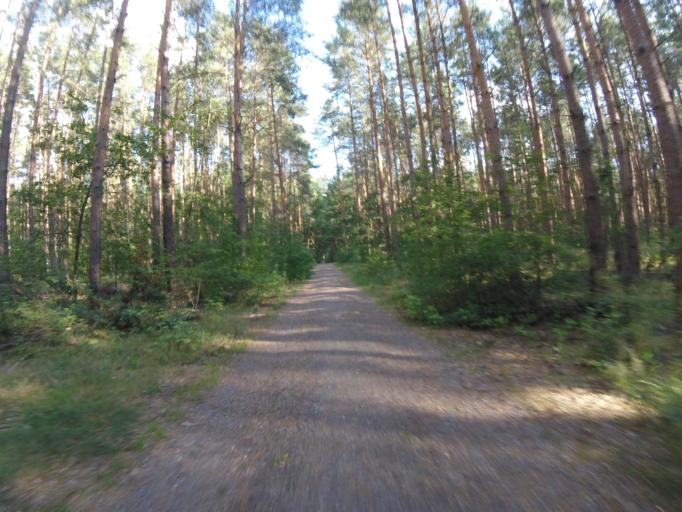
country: DE
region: Brandenburg
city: Schulzendorf
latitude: 52.3280
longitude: 13.5880
